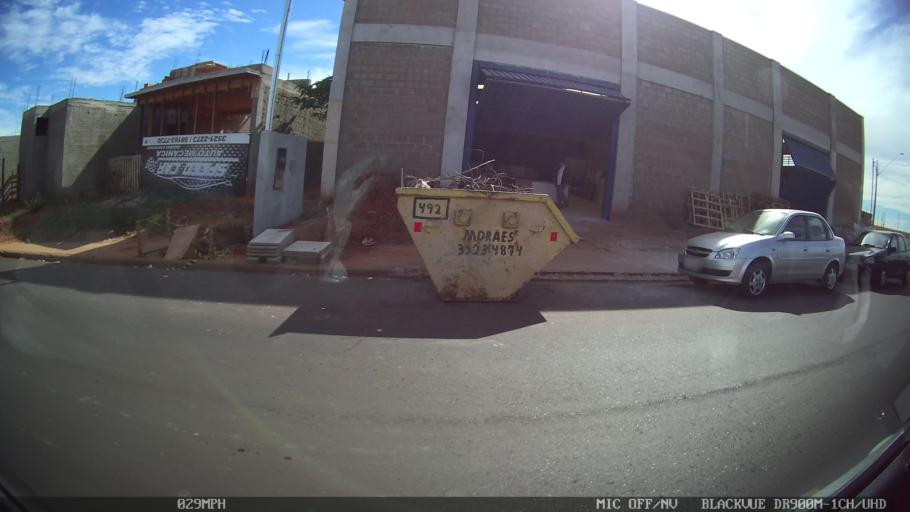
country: BR
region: Sao Paulo
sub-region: Catanduva
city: Catanduva
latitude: -21.1214
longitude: -48.9410
